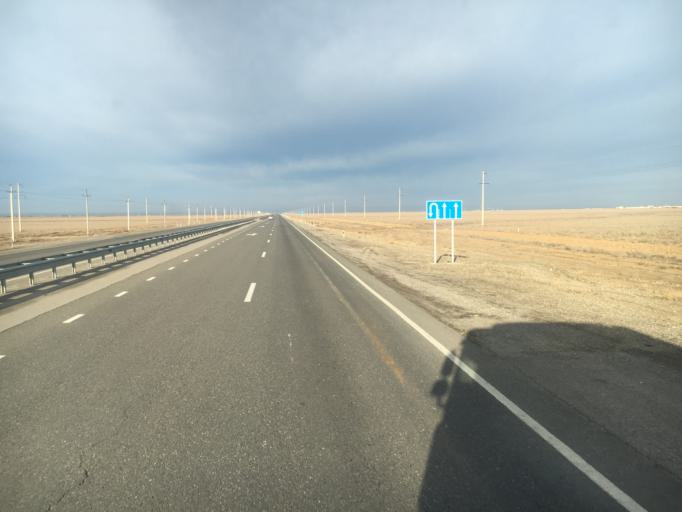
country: KZ
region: Ongtustik Qazaqstan
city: Turkestan
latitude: 43.4287
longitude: 67.9953
